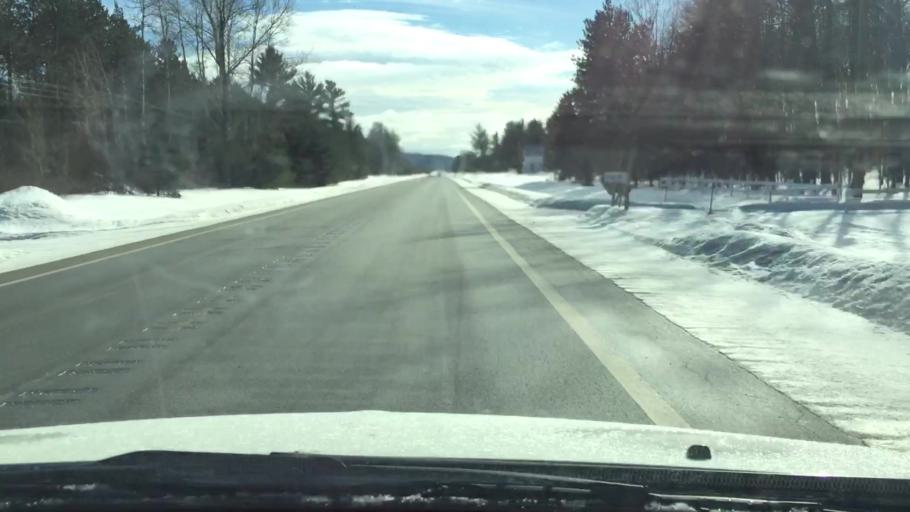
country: US
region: Michigan
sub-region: Antrim County
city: Mancelona
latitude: 44.9371
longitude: -85.0509
